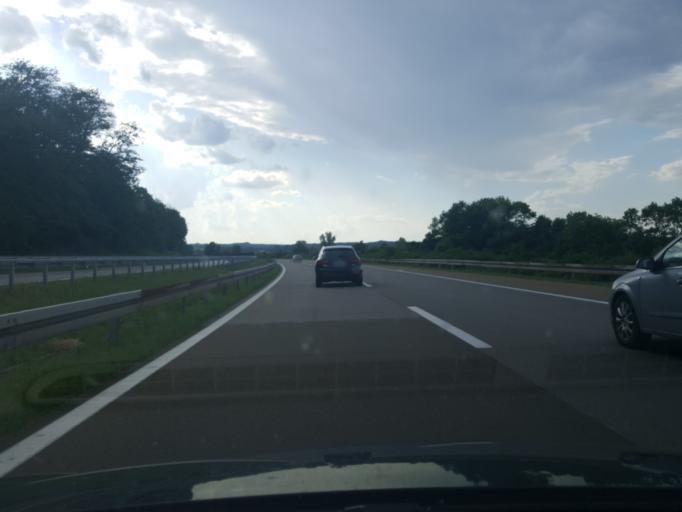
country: RS
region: Central Serbia
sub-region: Podunavski Okrug
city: Smederevo
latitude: 44.5852
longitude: 20.8666
